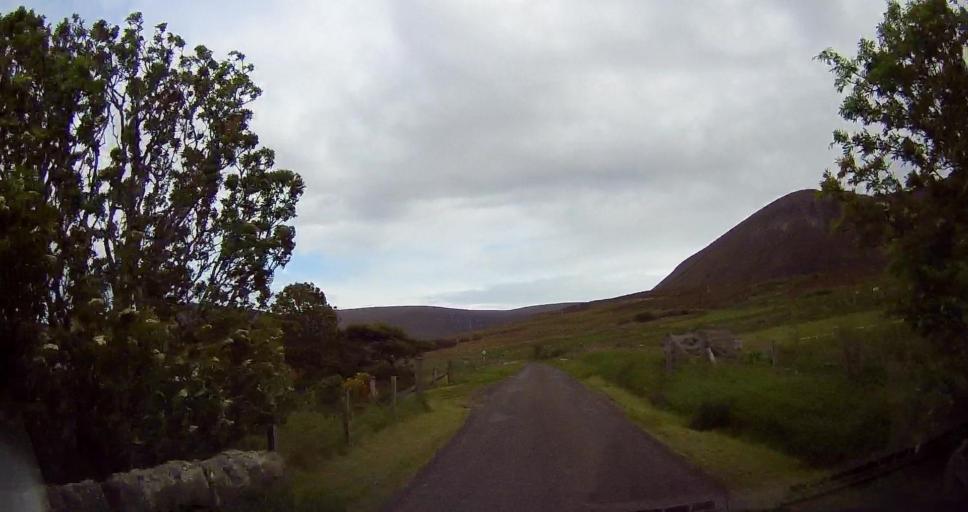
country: GB
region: Scotland
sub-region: Orkney Islands
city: Stromness
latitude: 58.9100
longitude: -3.3208
